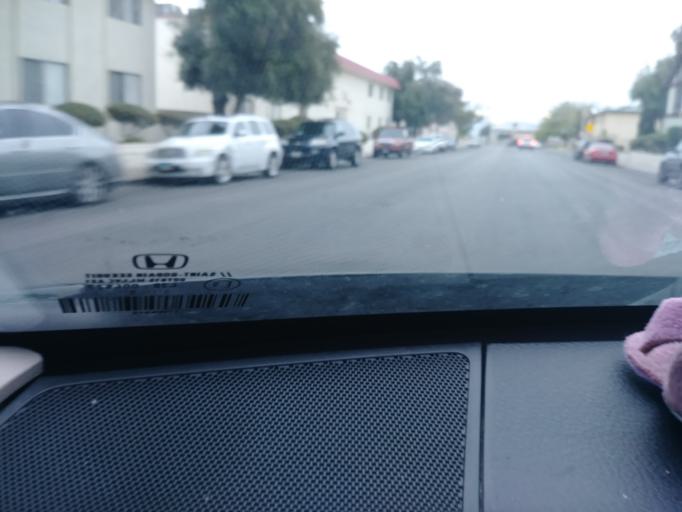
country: US
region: Nevada
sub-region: Clark County
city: Spring Valley
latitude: 36.1768
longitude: -115.2215
